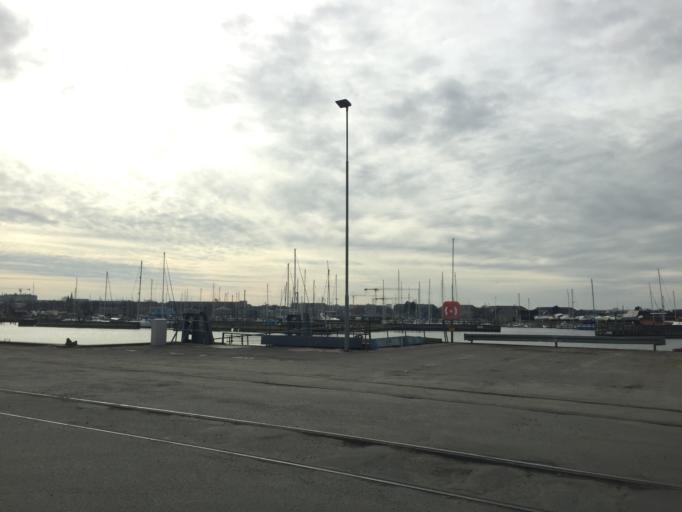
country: DK
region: Capital Region
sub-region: Gentofte Kommune
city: Charlottenlund
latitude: 55.7172
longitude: 12.5941
